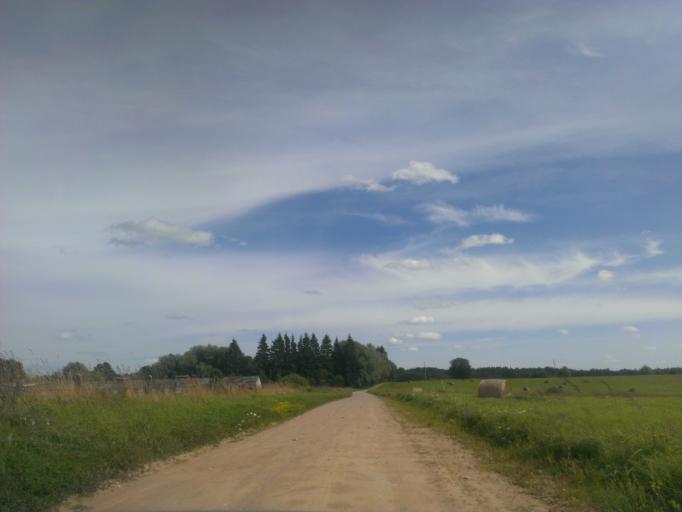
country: LV
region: Ligatne
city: Ligatne
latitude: 57.2252
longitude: 25.0008
